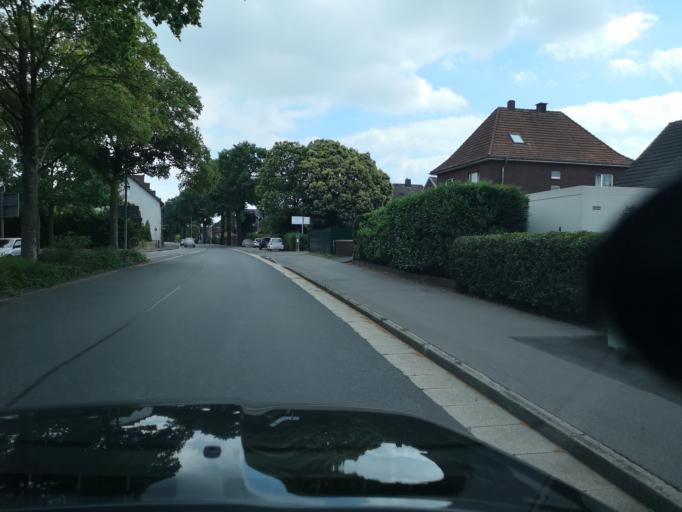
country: DE
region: North Rhine-Westphalia
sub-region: Regierungsbezirk Dusseldorf
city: Wesel
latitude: 51.6714
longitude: 6.6383
